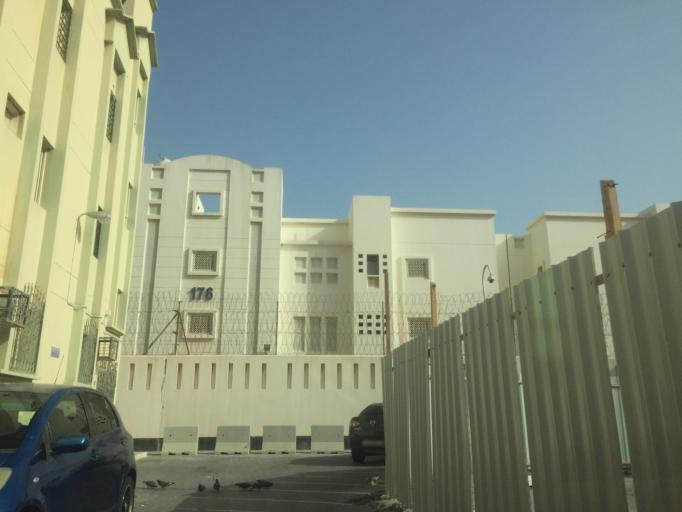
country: BH
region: Manama
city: Manama
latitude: 26.2207
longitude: 50.5752
